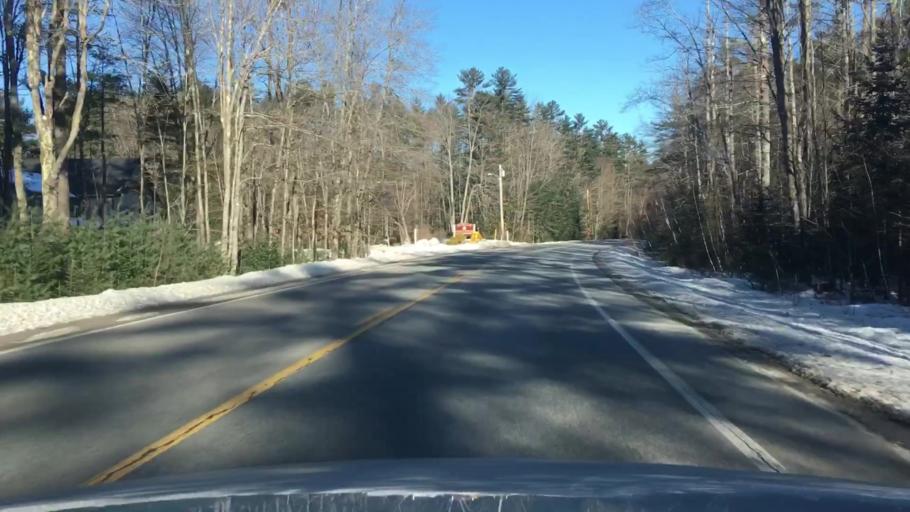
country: US
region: Maine
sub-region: Androscoggin County
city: Lisbon Falls
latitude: 43.9582
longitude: -70.1233
